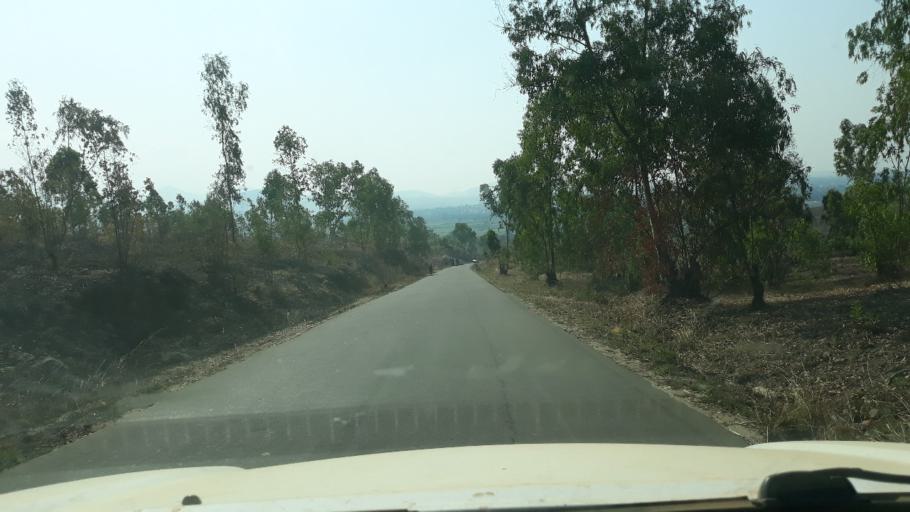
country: BI
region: Cibitoke
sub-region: Commune of Buganda
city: Buganda
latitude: -3.0990
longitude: 29.1310
